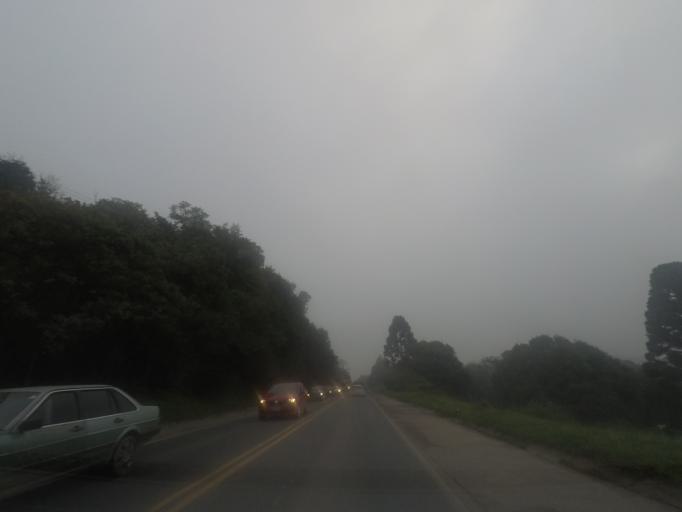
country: BR
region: Parana
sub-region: Almirante Tamandare
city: Almirante Tamandare
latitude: -25.3001
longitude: -49.3036
